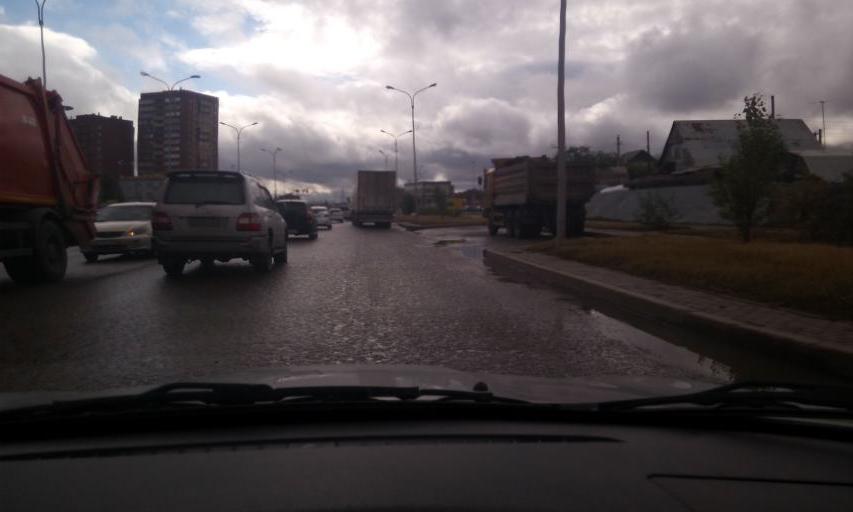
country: KZ
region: Astana Qalasy
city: Astana
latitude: 51.1828
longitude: 71.3756
